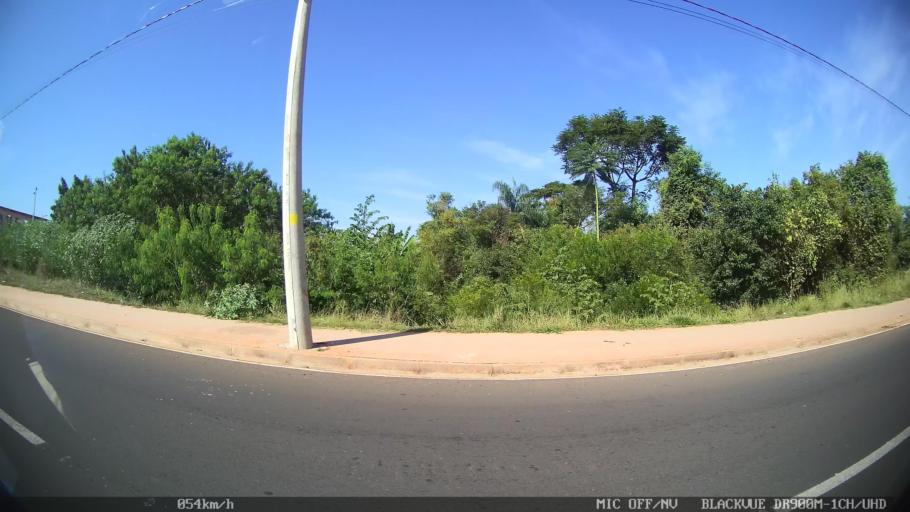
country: BR
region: Sao Paulo
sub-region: Sao Jose Do Rio Preto
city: Sao Jose do Rio Preto
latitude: -20.7629
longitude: -49.3671
